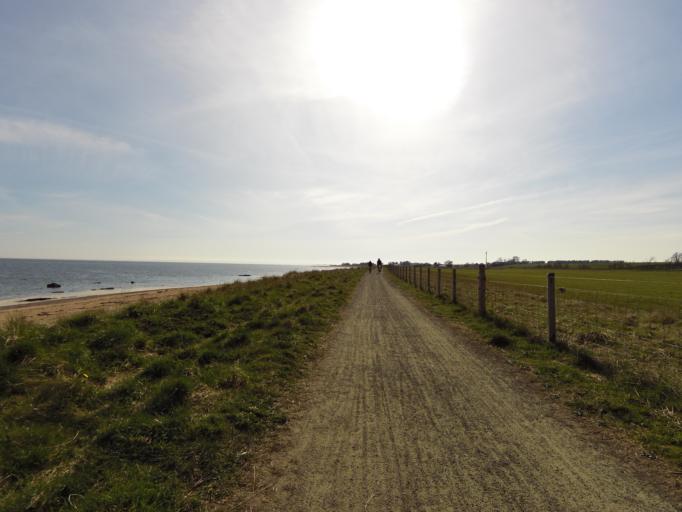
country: GB
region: Scotland
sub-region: Angus
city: Carnoustie
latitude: 56.5197
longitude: -2.6570
